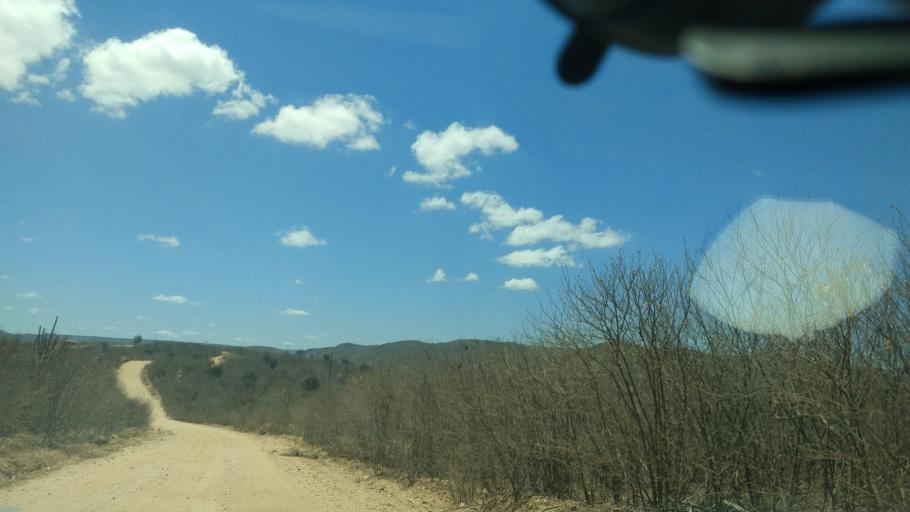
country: BR
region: Rio Grande do Norte
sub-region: Cerro Cora
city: Cerro Cora
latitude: -6.0114
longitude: -36.3015
